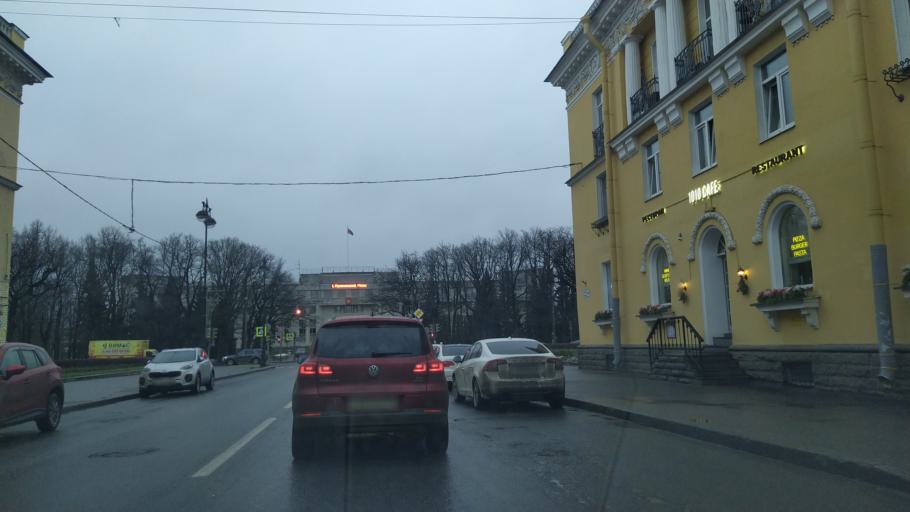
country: RU
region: St.-Petersburg
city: Pushkin
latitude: 59.7213
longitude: 30.4154
